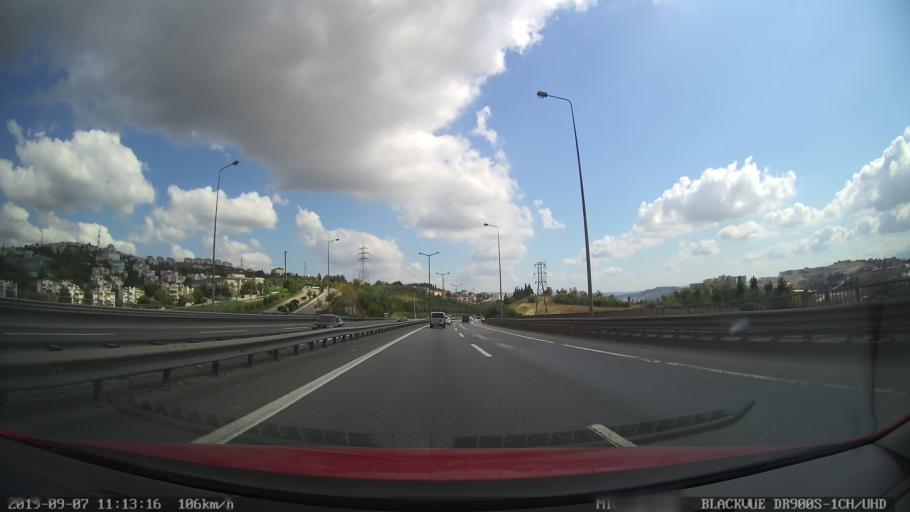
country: TR
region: Kocaeli
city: Izmit
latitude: 40.7821
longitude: 29.9442
